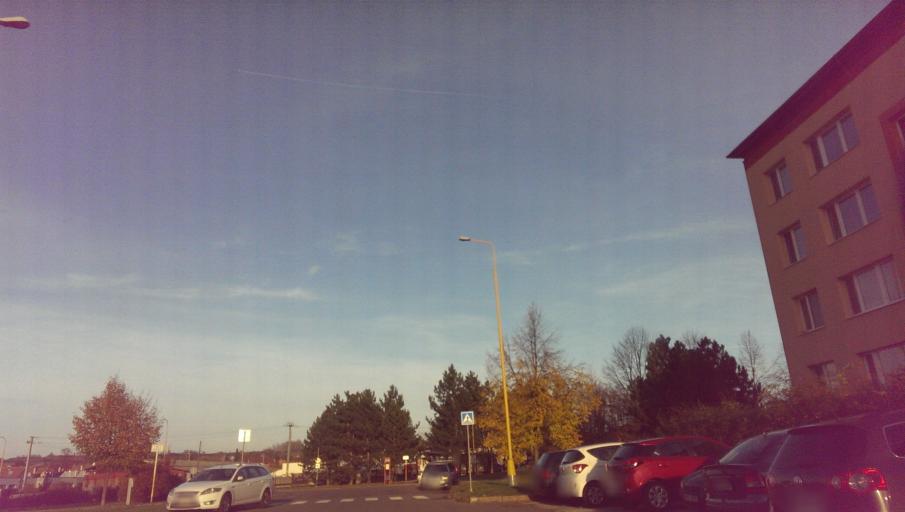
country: CZ
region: Zlin
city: Kunovice
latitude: 49.0590
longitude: 17.4836
